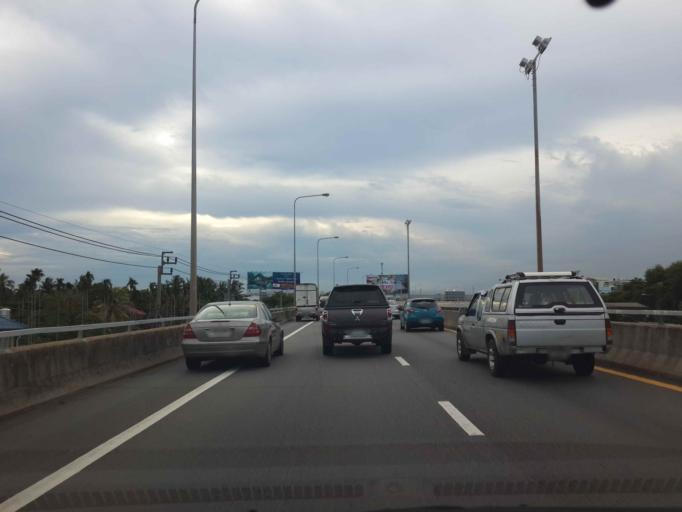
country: TH
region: Bangkok
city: Chom Thong
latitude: 13.6752
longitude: 100.4819
